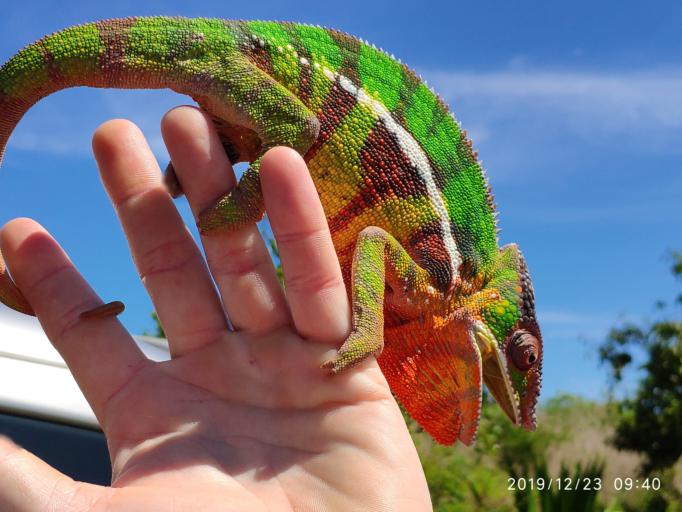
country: MG
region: Diana
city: Sadjoavato
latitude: -12.4689
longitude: 49.2232
